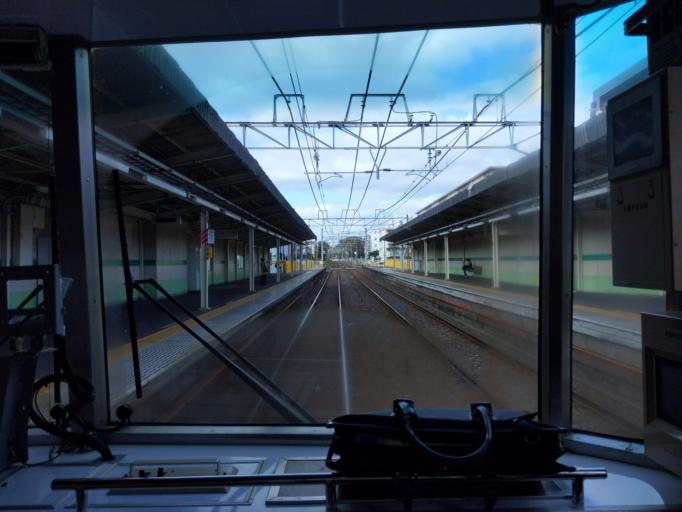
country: JP
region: Chiba
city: Funabashi
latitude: 35.7154
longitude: 140.0428
